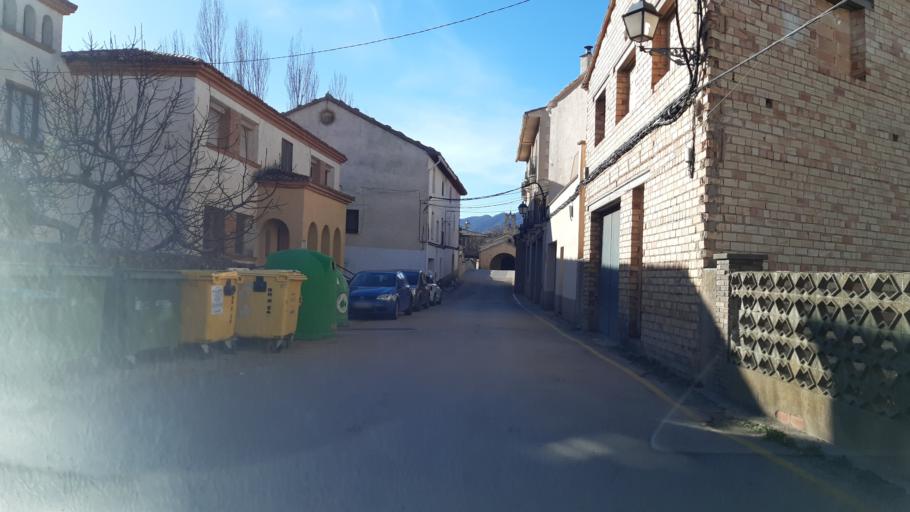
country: ES
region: Aragon
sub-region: Provincia de Teruel
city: Valderrobres
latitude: 40.8312
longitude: 0.1809
